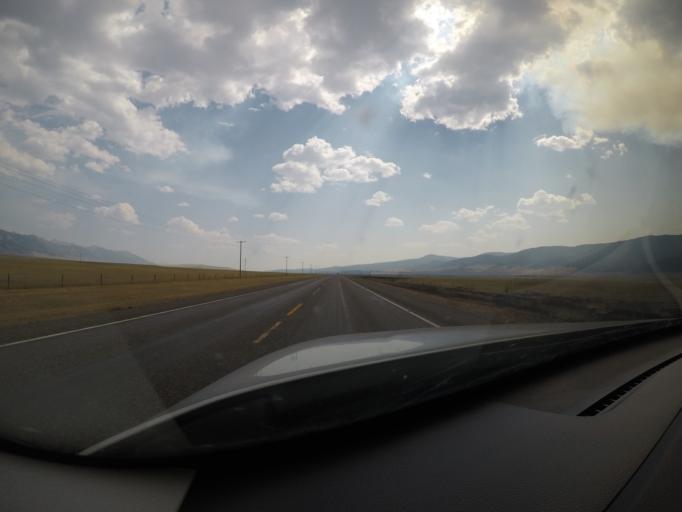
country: US
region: Montana
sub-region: Gallatin County
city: Big Sky
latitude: 45.0226
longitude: -111.6483
